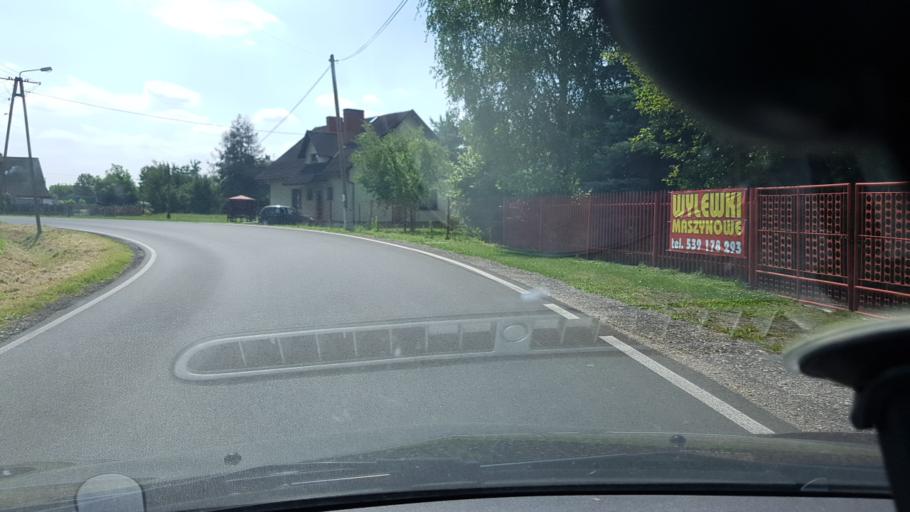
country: PL
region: Lesser Poland Voivodeship
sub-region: Powiat oswiecimski
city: Brzezinka
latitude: 50.0486
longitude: 19.1831
